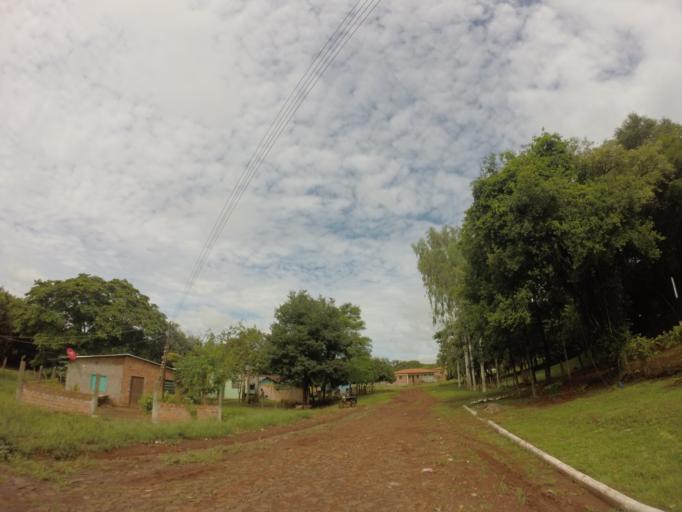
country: PY
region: Alto Parana
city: Ciudad del Este
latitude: -25.4138
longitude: -54.6404
